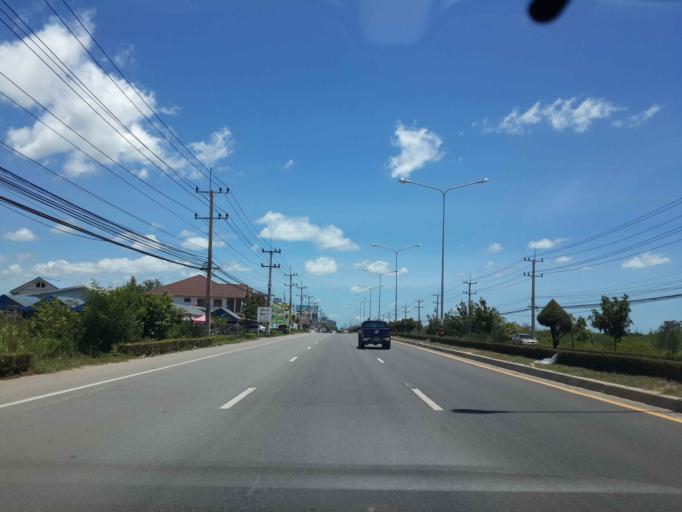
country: TH
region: Phetchaburi
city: Cha-am
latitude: 12.6926
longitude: 99.9530
